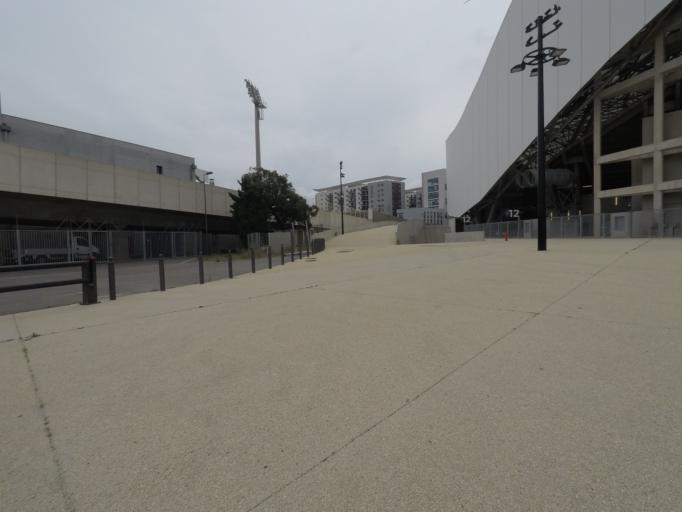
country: FR
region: Provence-Alpes-Cote d'Azur
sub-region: Departement des Bouches-du-Rhone
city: Marseille 08
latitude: 43.2698
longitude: 5.3979
